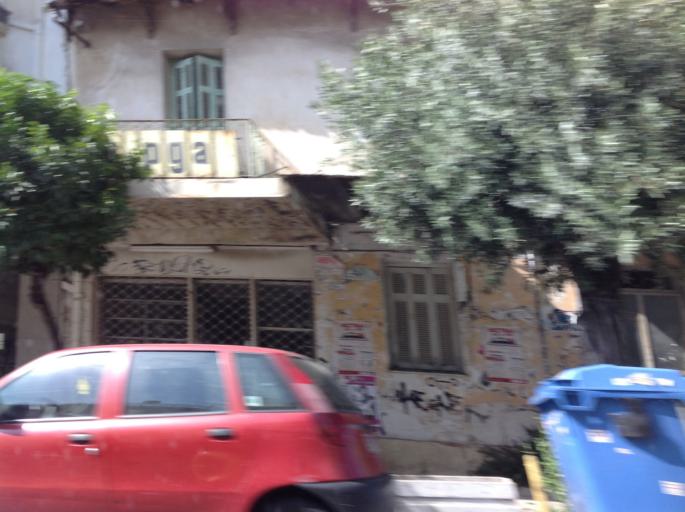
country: GR
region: Attica
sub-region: Nomarchia Athinas
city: Kaisariani
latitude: 37.9681
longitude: 23.7602
